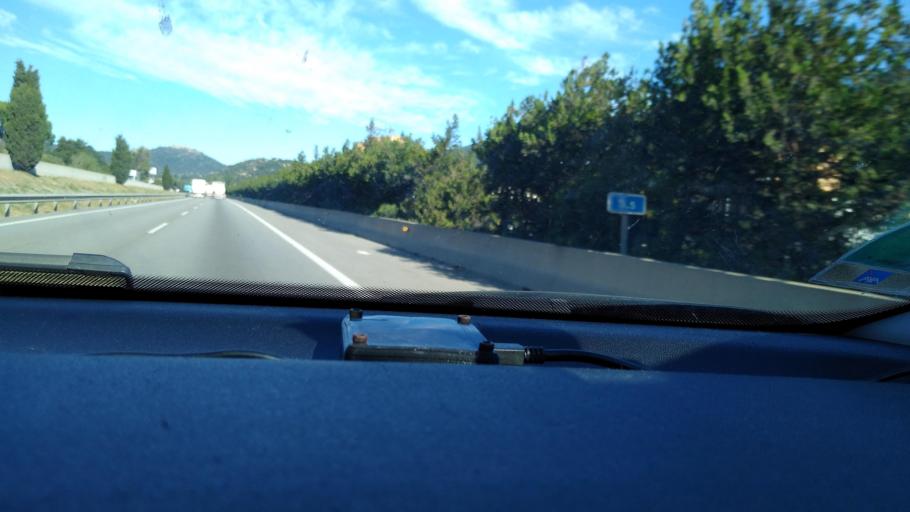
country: ES
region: Catalonia
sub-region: Provincia de Girona
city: la Jonquera
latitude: 42.4175
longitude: 2.8712
